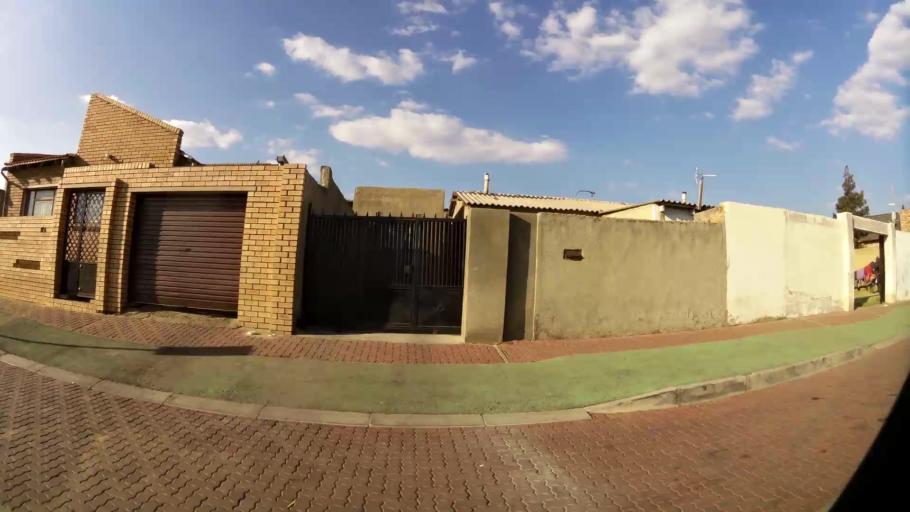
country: ZA
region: Gauteng
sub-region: City of Johannesburg Metropolitan Municipality
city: Soweto
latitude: -26.2184
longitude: 27.8860
